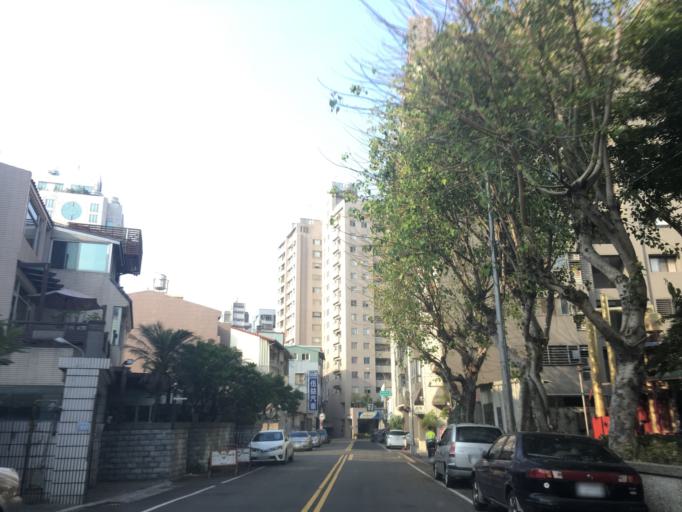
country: TW
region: Taiwan
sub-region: Taichung City
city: Taichung
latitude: 24.1694
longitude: 120.6840
